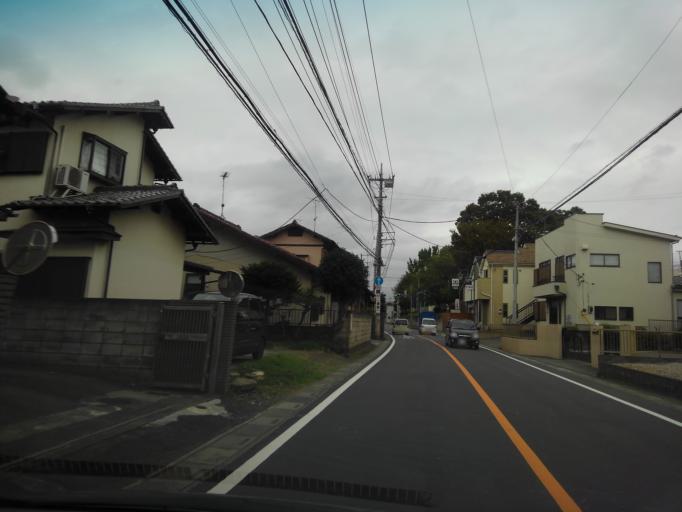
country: JP
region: Saitama
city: Tokorozawa
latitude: 35.7905
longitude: 139.4368
